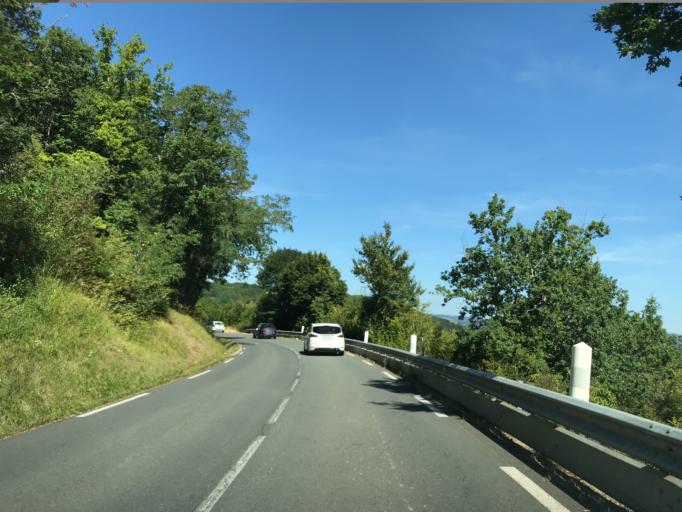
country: FR
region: Limousin
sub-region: Departement de la Correze
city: Larche
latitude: 45.1006
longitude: 1.3936
